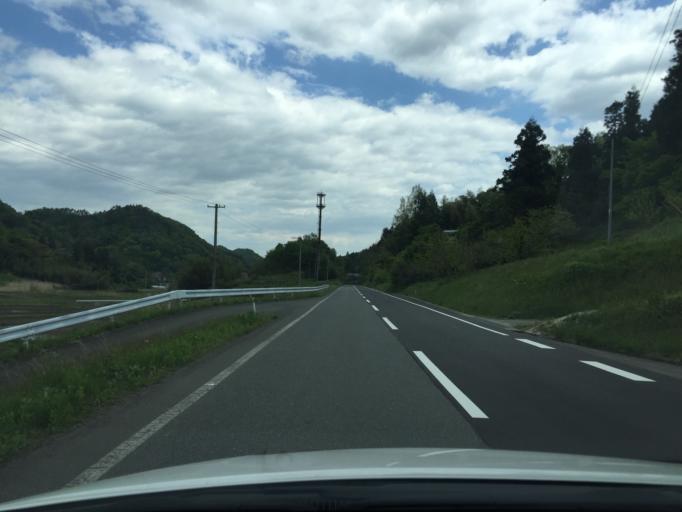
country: JP
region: Fukushima
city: Hobaramachi
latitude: 37.7327
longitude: 140.5554
